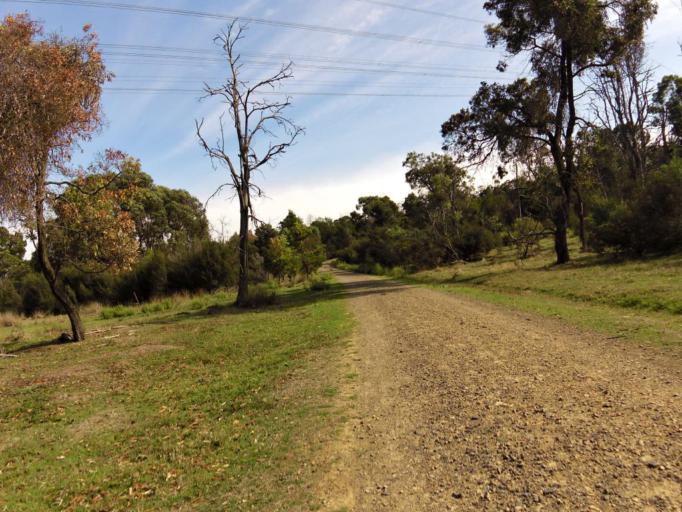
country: AU
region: Victoria
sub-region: Casey
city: Endeavour Hills
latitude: -37.9555
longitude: 145.2614
